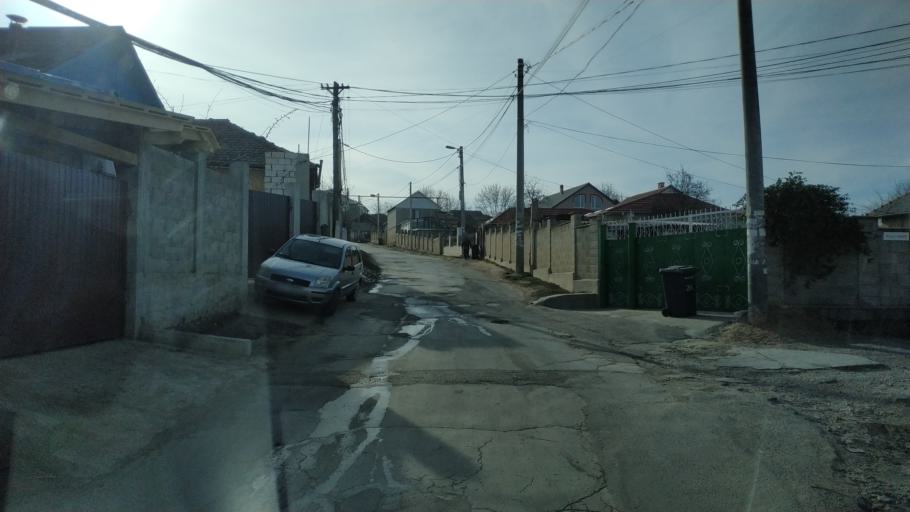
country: MD
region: Chisinau
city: Vatra
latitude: 47.0718
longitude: 28.6783
